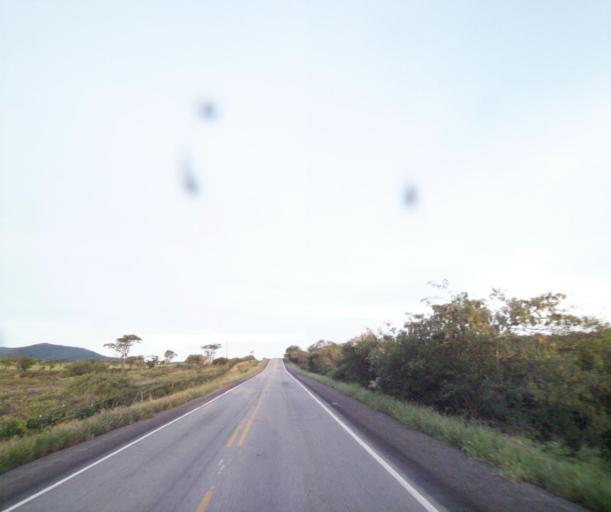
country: BR
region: Bahia
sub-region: Brumado
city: Brumado
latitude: -14.2583
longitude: -41.7806
